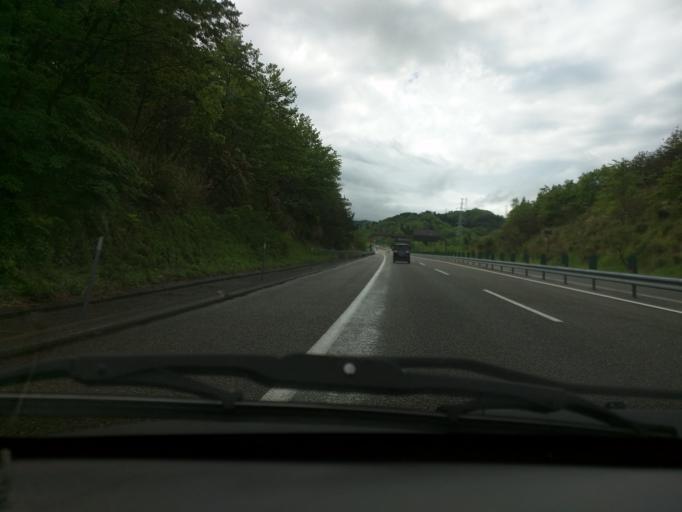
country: JP
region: Niigata
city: Joetsu
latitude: 37.1343
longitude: 138.2133
